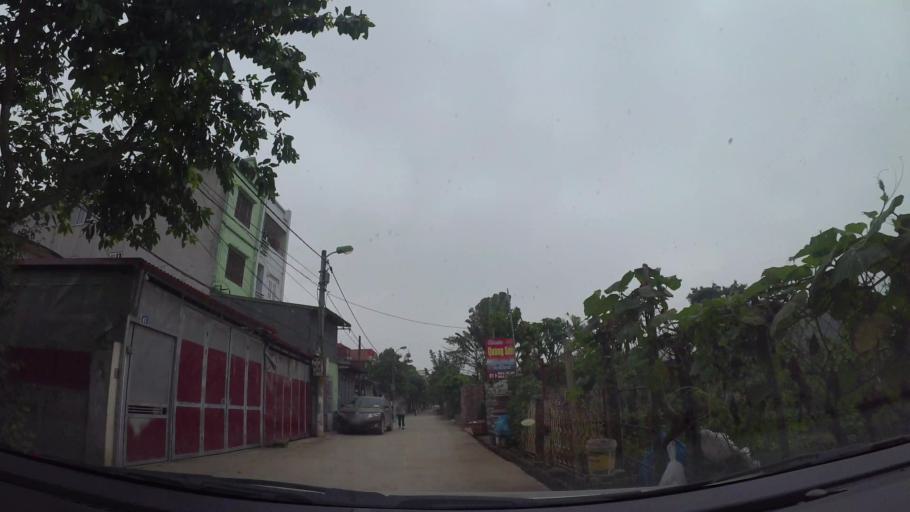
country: VN
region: Ha Noi
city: Tay Ho
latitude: 21.0757
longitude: 105.8272
